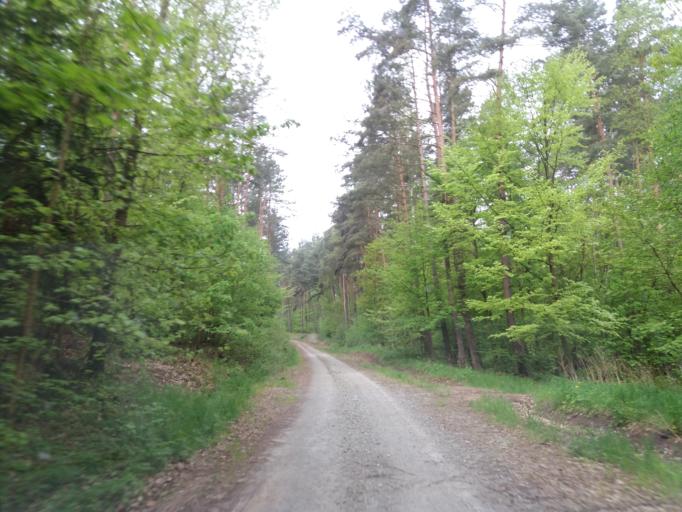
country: PL
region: West Pomeranian Voivodeship
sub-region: Powiat choszczenski
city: Bierzwnik
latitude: 53.0182
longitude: 15.5720
